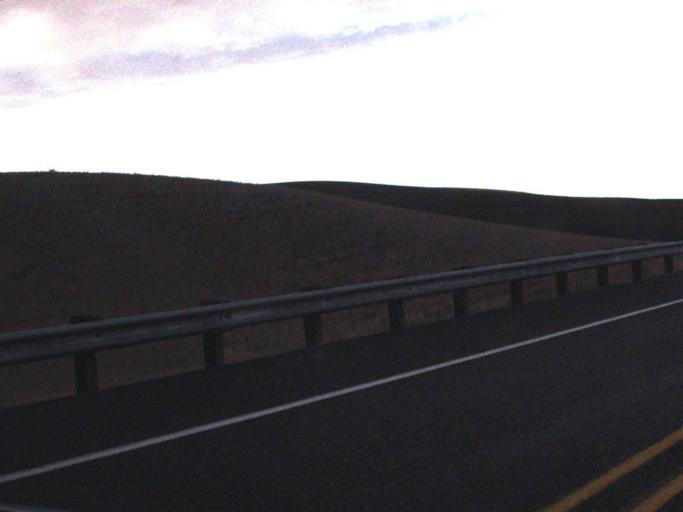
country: US
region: Washington
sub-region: Garfield County
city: Pomeroy
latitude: 46.5614
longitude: -117.7743
